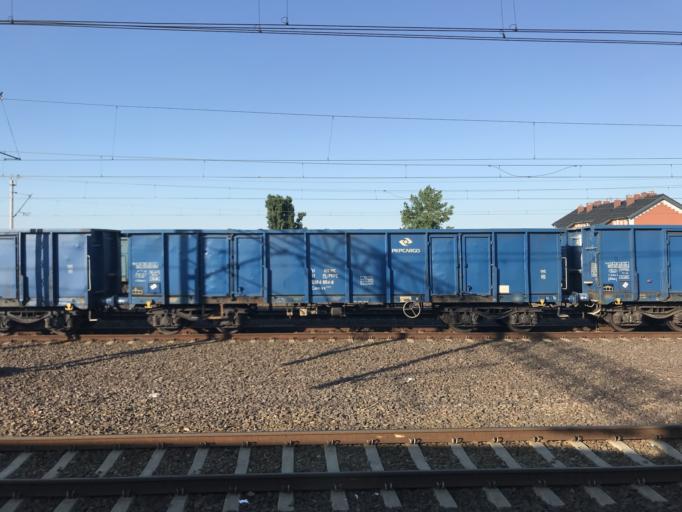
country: PL
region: Pomeranian Voivodeship
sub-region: Powiat tczewski
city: Tczew
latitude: 54.0988
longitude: 18.7879
